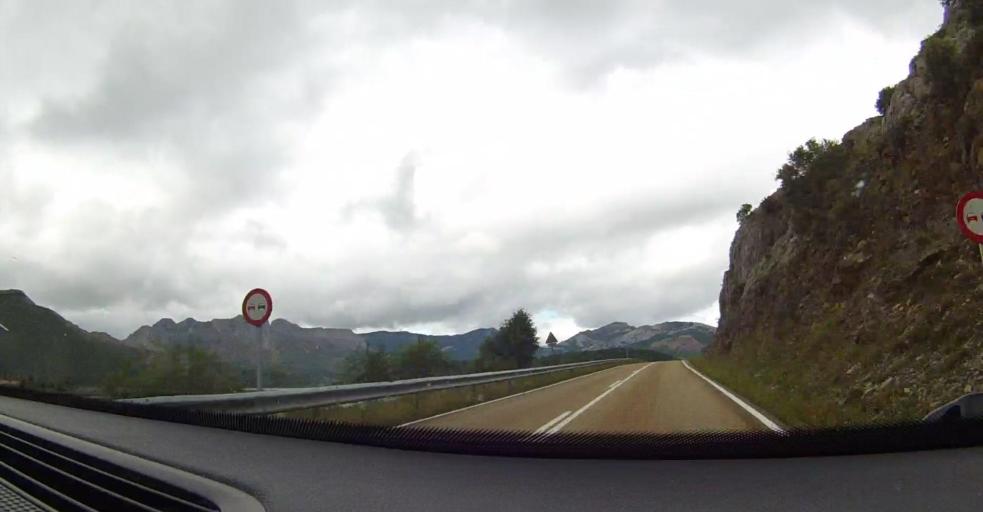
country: ES
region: Castille and Leon
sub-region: Provincia de Leon
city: Bonar
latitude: 42.9285
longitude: -5.2821
